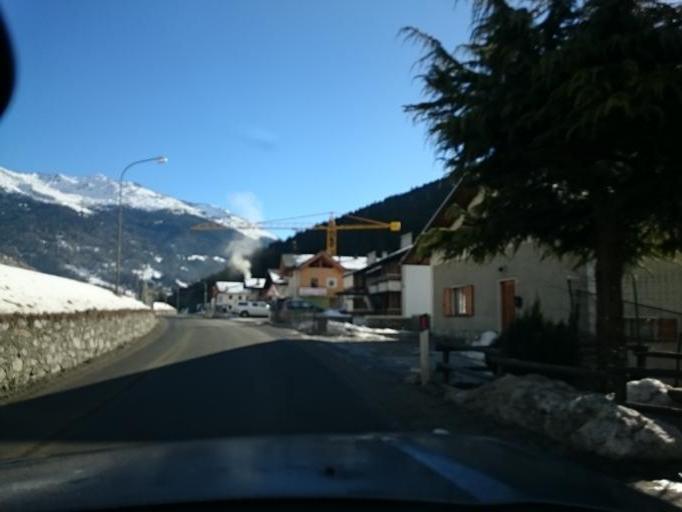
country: IT
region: Lombardy
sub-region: Provincia di Sondrio
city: San Nicolo
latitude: 46.4633
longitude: 10.4013
